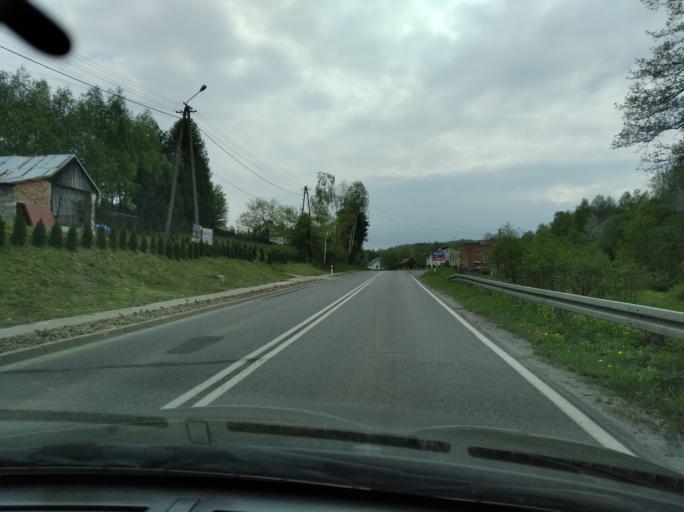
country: PL
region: Lesser Poland Voivodeship
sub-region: Powiat tarnowski
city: Tarnowiec
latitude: 49.9570
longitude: 20.9995
